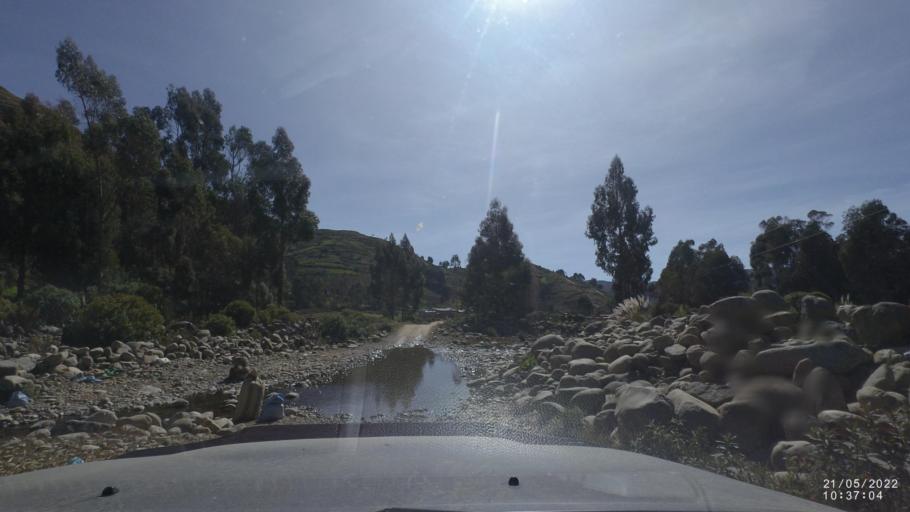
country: BO
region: Cochabamba
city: Colomi
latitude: -17.3138
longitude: -65.9216
